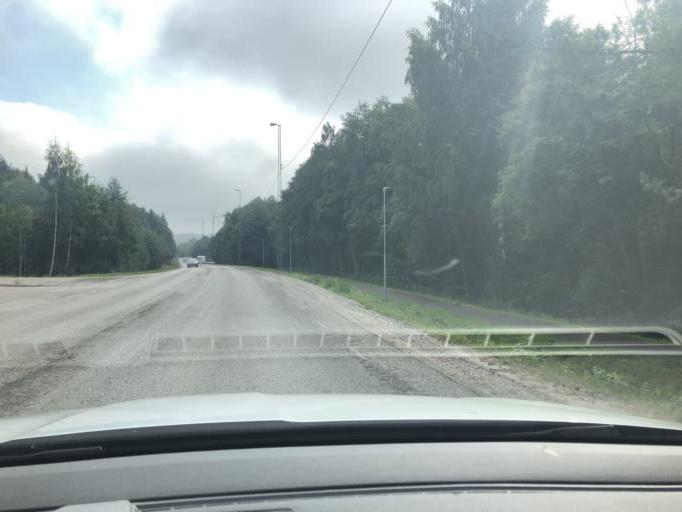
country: SE
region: Vaesternorrland
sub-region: Sundsvalls Kommun
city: Sundsvall
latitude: 62.4114
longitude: 17.3198
